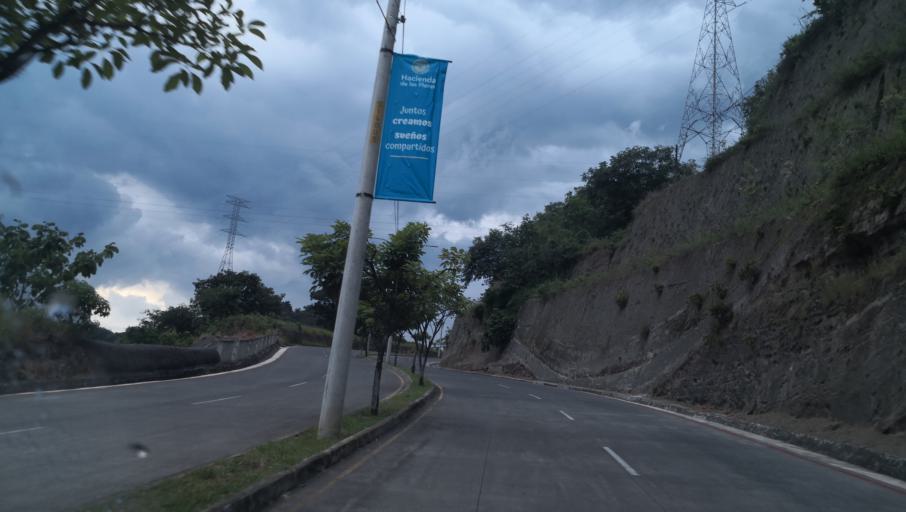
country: GT
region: Guatemala
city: Villa Nueva
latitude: 14.5541
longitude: -90.5941
